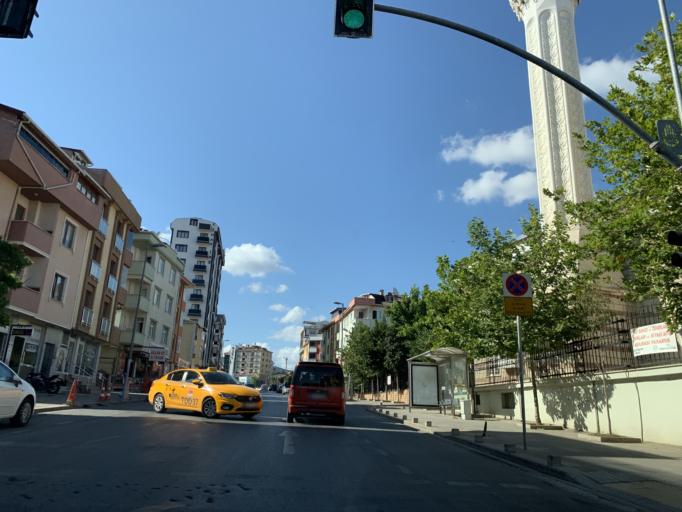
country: TR
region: Istanbul
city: Pendik
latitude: 40.8876
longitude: 29.2729
